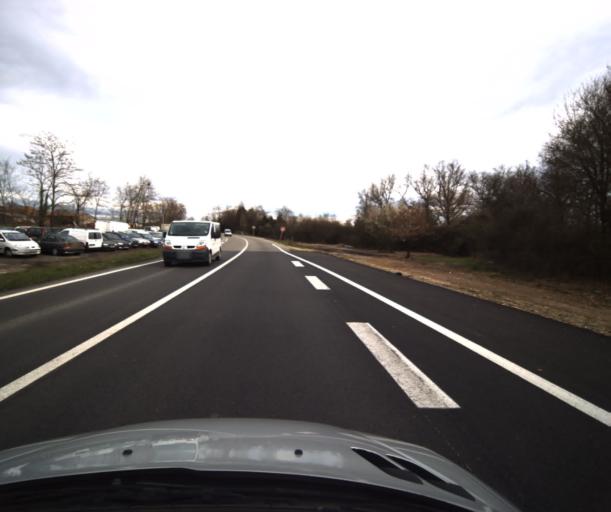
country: FR
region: Midi-Pyrenees
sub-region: Departement du Tarn-et-Garonne
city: Montauban
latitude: 44.0305
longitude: 1.3908
